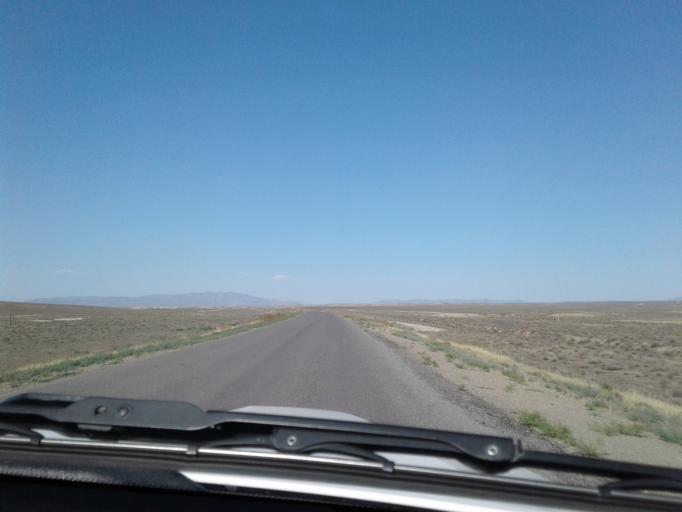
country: TM
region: Balkan
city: Magtymguly
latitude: 38.6066
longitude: 56.2065
